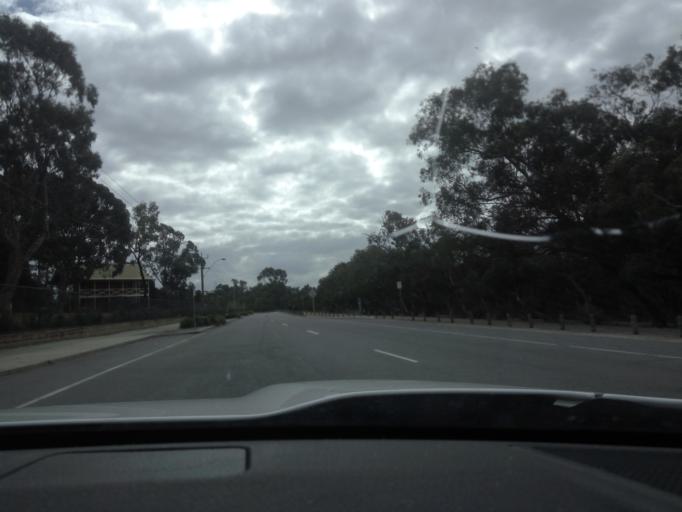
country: AU
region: Western Australia
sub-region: City of Cockburn
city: Bibra Lake
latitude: -32.0953
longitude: 115.8200
